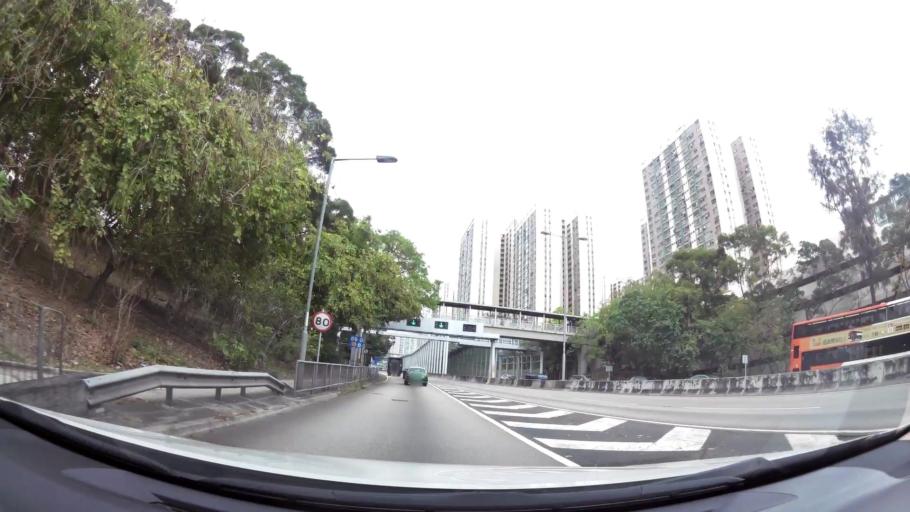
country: HK
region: Tsuen Wan
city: Tsuen Wan
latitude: 22.3764
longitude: 114.1227
